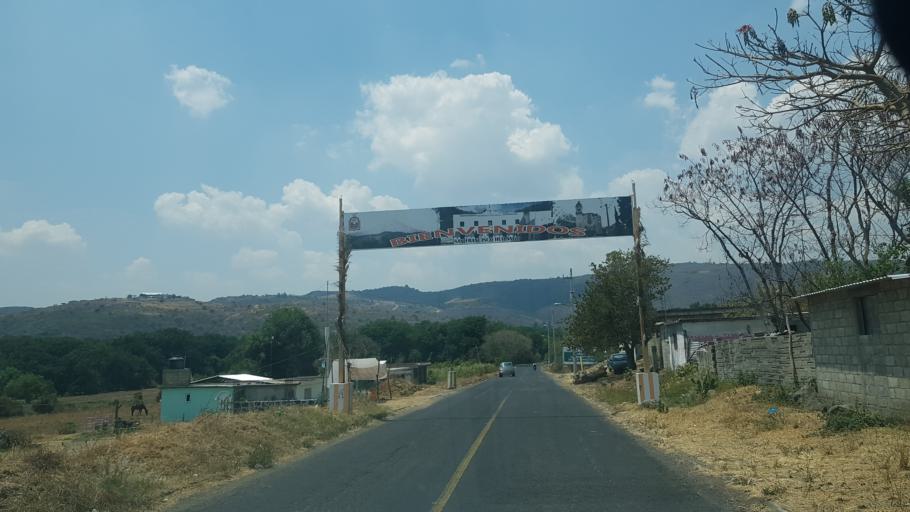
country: MX
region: Puebla
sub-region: Atzitzihuacan
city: Santiago Atzitzihuacan
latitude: 18.8391
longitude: -98.5792
